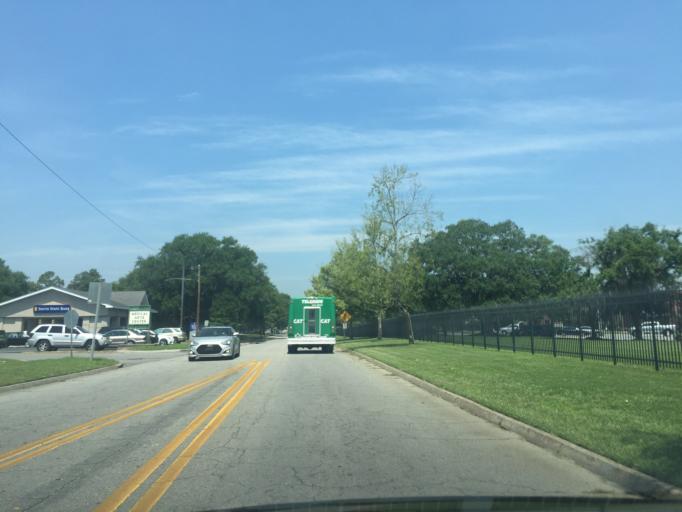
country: US
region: Georgia
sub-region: Chatham County
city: Thunderbolt
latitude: 32.0320
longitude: -81.0923
